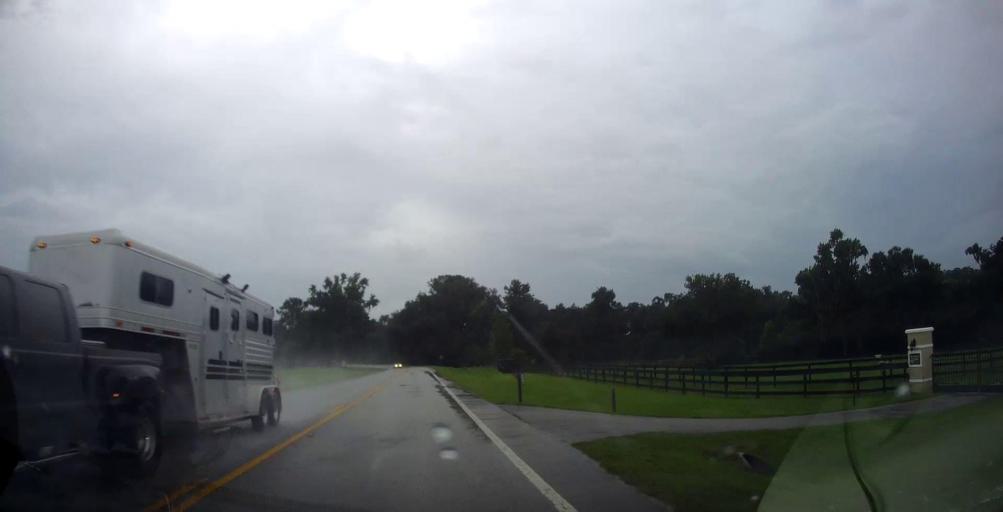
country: US
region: Florida
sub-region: Marion County
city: Citra
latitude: 29.3760
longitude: -82.2516
